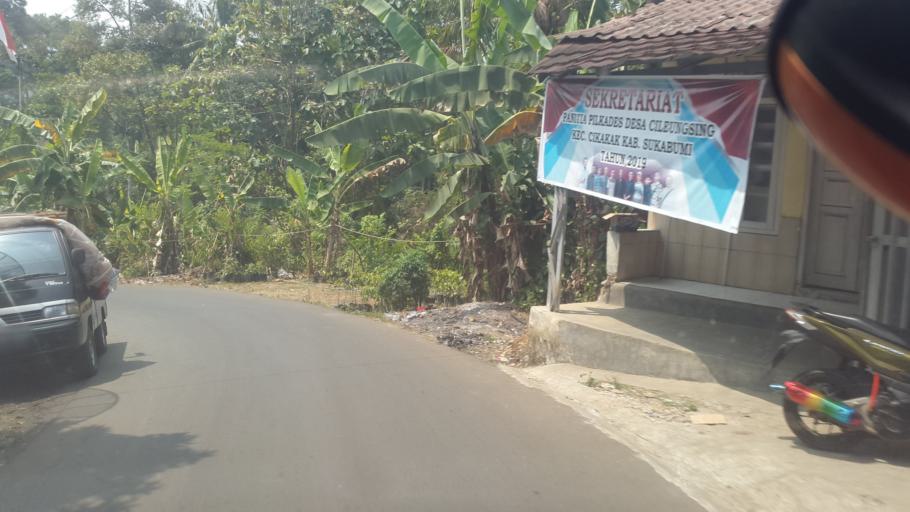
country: ID
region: West Java
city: Cimaja
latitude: -6.9213
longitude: 106.5234
